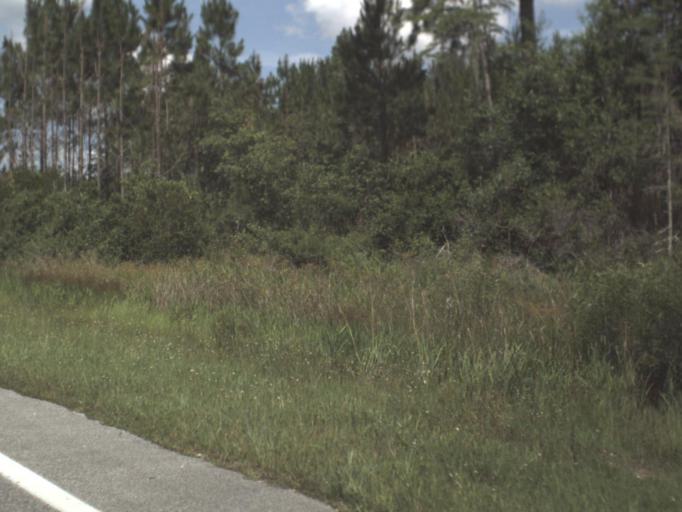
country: US
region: Florida
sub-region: Levy County
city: Bronson
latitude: 29.4260
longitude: -82.6686
